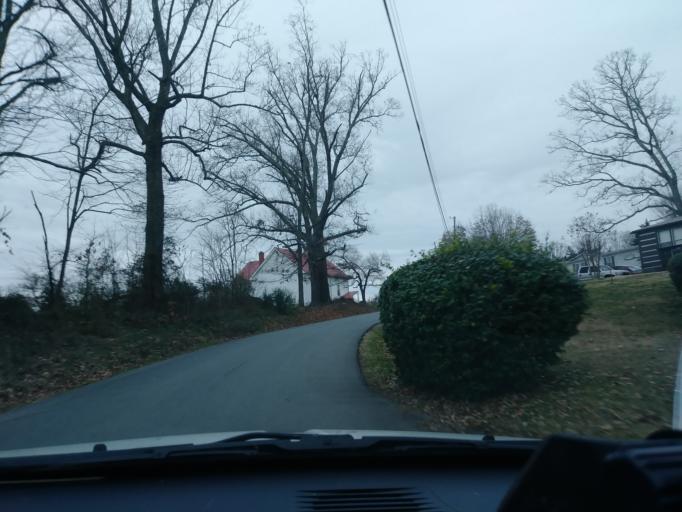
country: US
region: Tennessee
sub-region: Greene County
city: Greeneville
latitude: 36.0753
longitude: -82.8853
